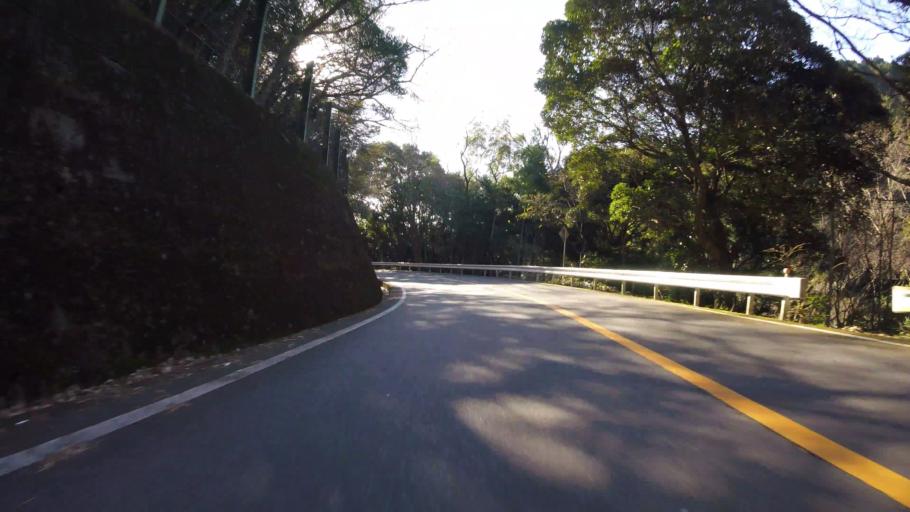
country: JP
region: Shizuoka
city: Atami
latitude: 35.1094
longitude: 139.0606
